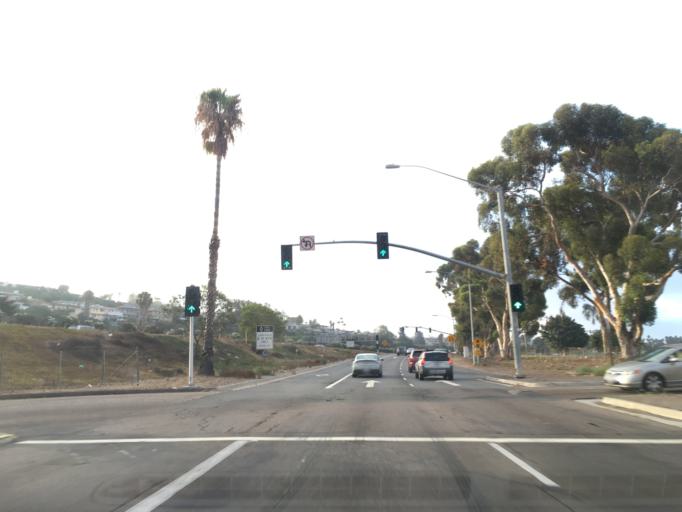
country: US
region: California
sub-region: San Diego County
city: La Jolla
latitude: 32.7985
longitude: -117.2113
